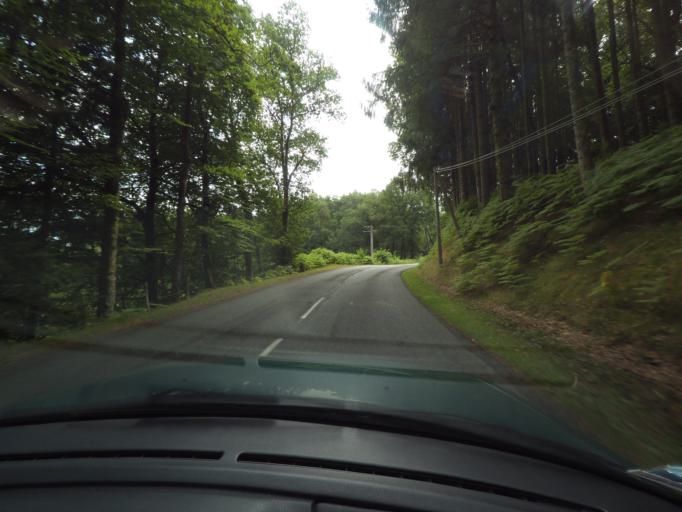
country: FR
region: Limousin
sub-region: Departement de la Haute-Vienne
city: Eymoutiers
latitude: 45.7195
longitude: 1.8628
